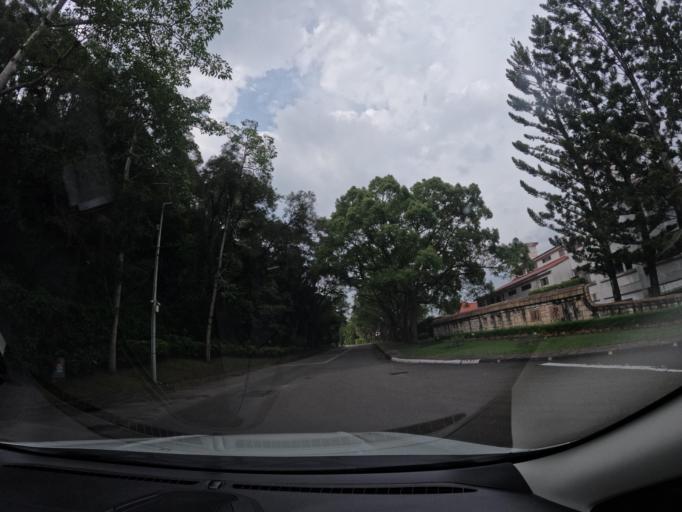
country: TW
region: Taiwan
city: Daxi
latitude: 24.8887
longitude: 121.3220
